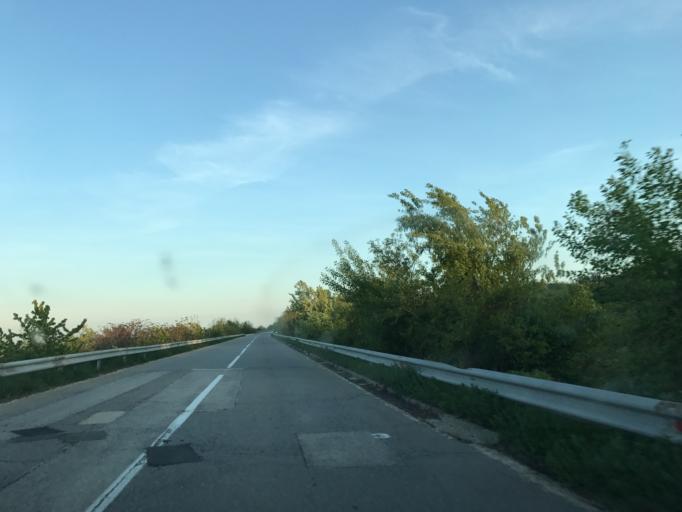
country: RO
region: Mehedinti
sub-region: Comuna Gogosu
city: Ostrovu Mare
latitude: 44.4189
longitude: 22.4830
